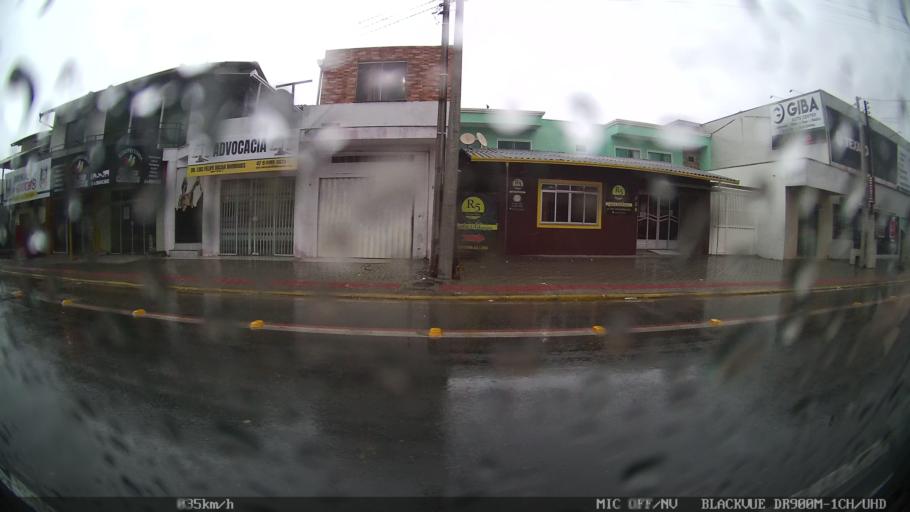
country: BR
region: Santa Catarina
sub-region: Navegantes
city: Navegantes
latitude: -26.8857
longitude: -48.6555
